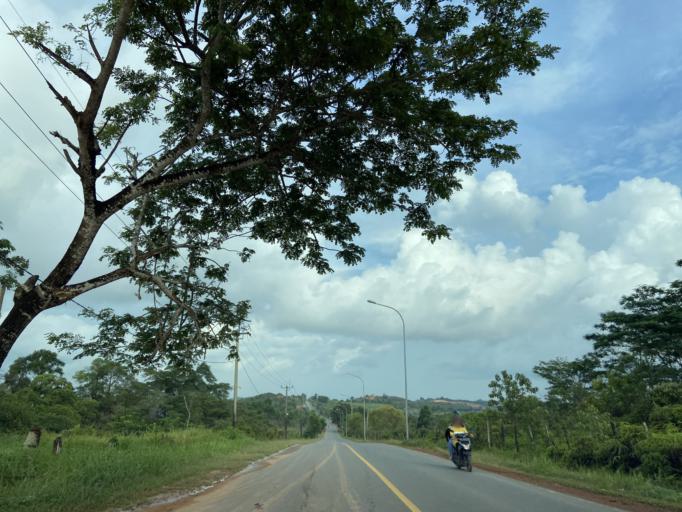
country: ID
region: Riau Islands
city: Tanjungpinang
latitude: 0.9368
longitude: 104.0960
